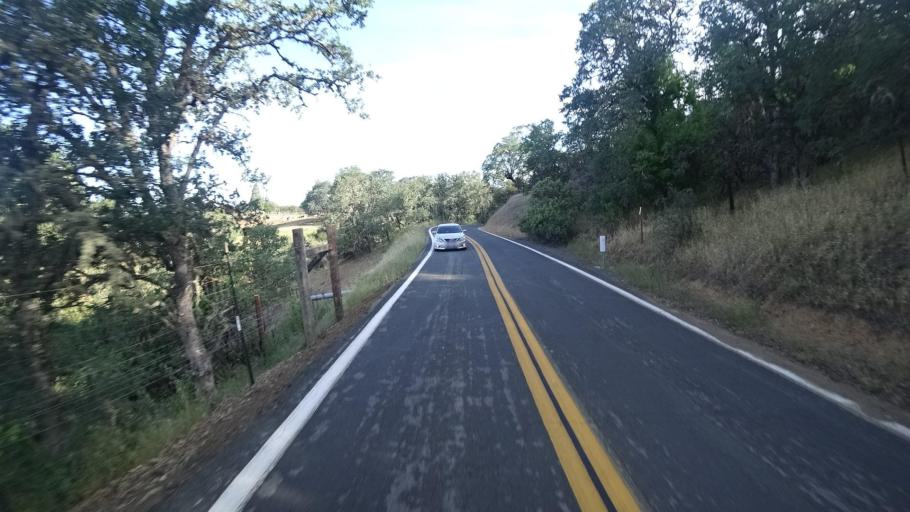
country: US
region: California
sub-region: Lake County
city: North Lakeport
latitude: 39.0705
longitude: -122.9283
